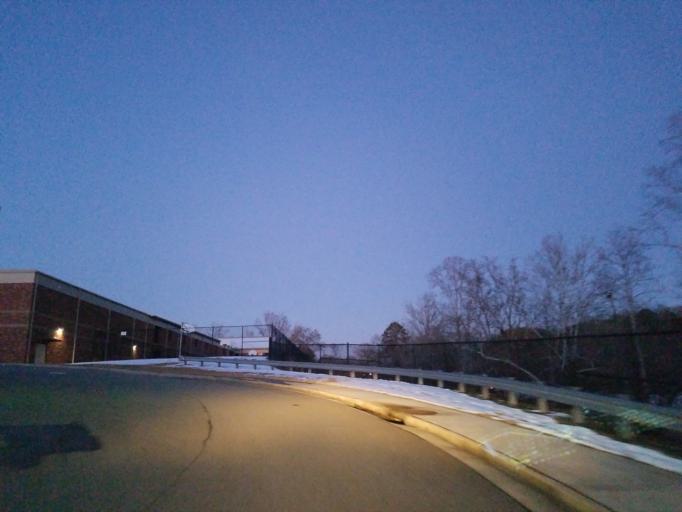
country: US
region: Georgia
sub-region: Cherokee County
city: Ball Ground
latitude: 34.3311
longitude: -84.3847
